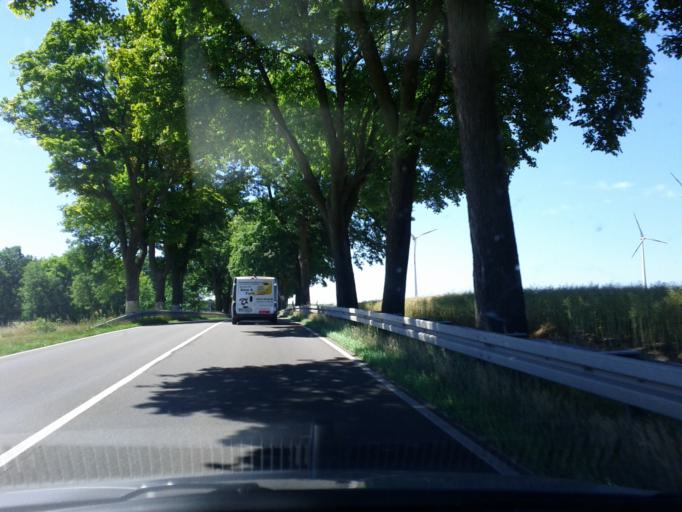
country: DE
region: Brandenburg
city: Rehfelde
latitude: 52.4802
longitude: 13.9422
